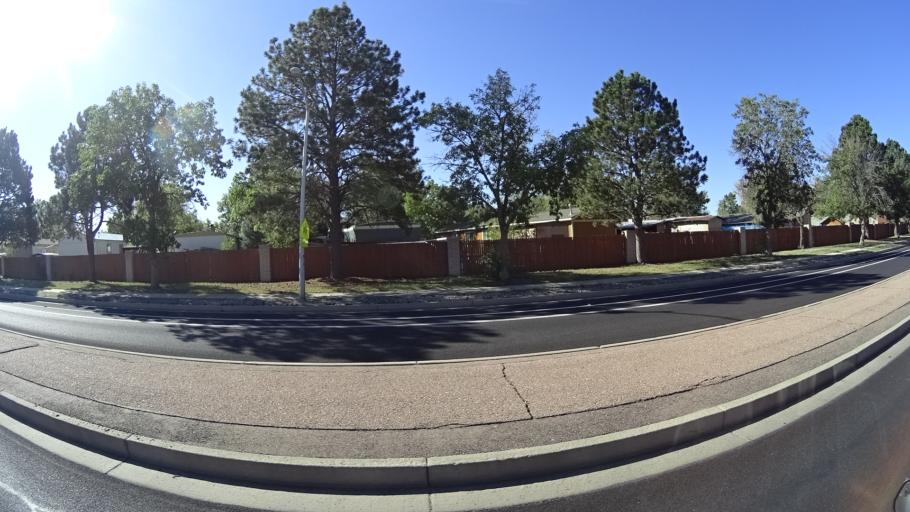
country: US
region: Colorado
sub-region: El Paso County
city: Stratmoor
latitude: 38.7990
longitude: -104.7363
